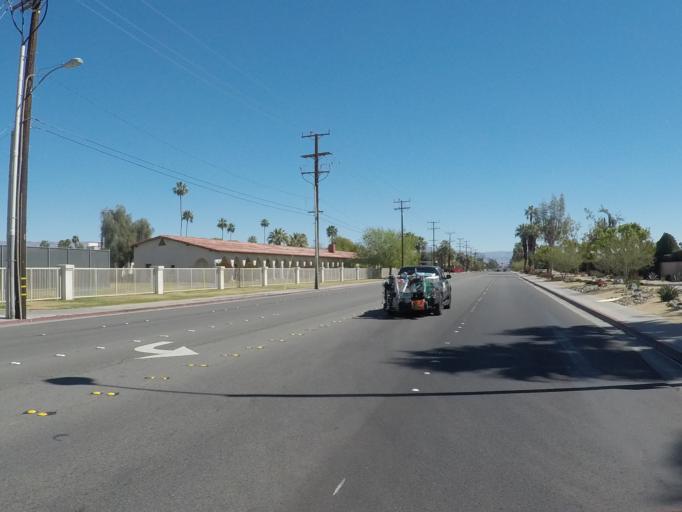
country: US
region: California
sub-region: Riverside County
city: Palm Springs
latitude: 33.8159
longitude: -116.5238
